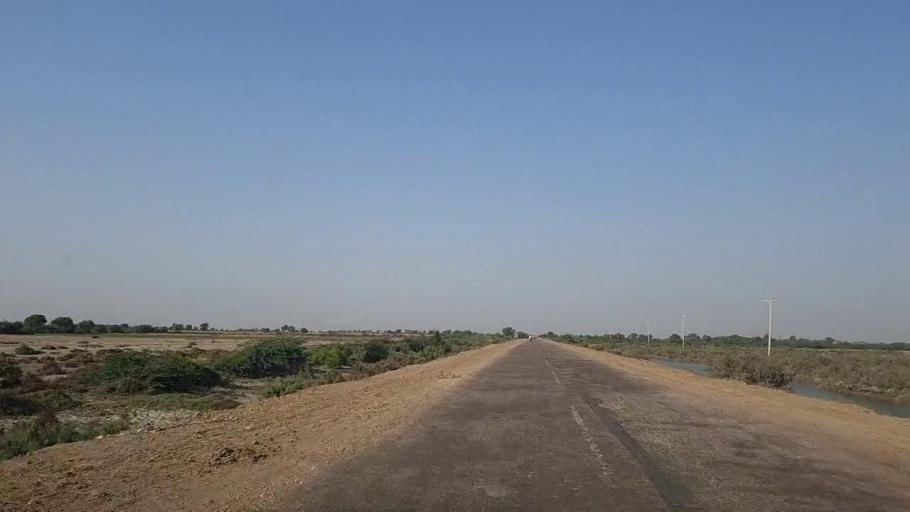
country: PK
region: Sindh
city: Mirpur Batoro
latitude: 24.6178
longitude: 68.4055
